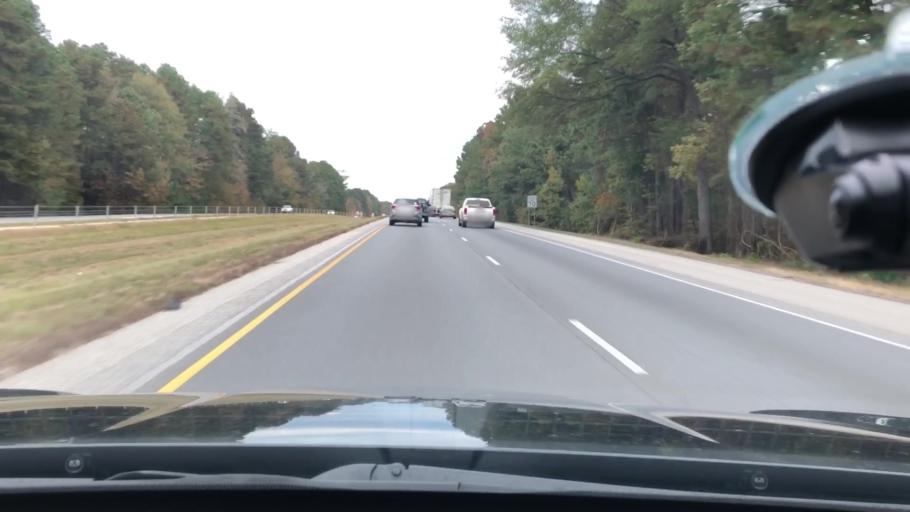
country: US
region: Arkansas
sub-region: Clark County
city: Arkadelphia
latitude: 34.1272
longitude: -93.0882
